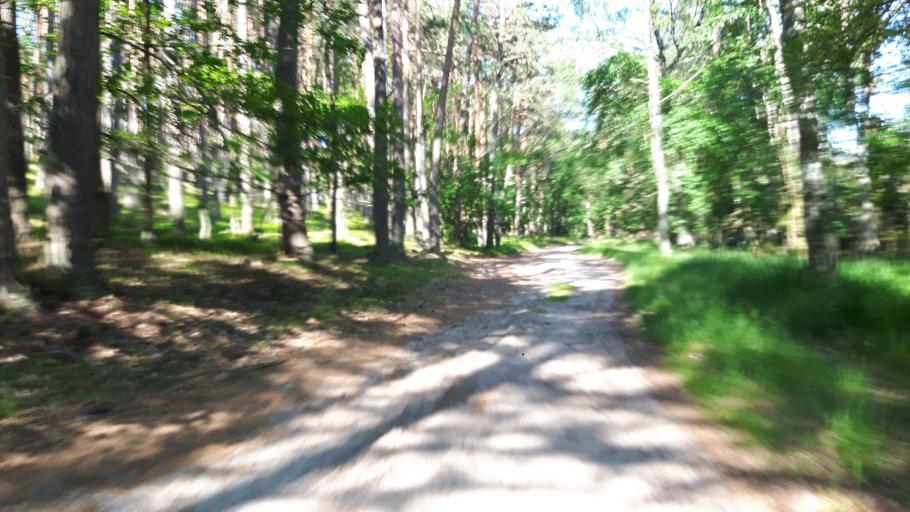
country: PL
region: Pomeranian Voivodeship
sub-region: Powiat leborski
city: Leba
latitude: 54.7031
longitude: 17.5175
